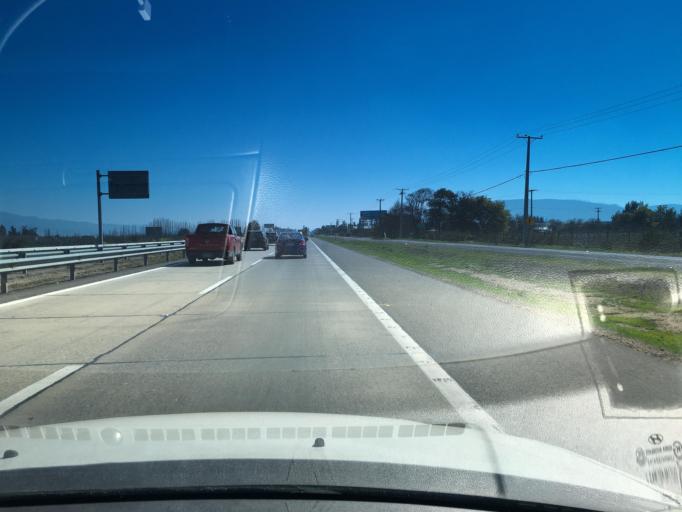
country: CL
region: Valparaiso
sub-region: Provincia de Marga Marga
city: Villa Alemana
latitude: -33.3566
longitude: -71.3306
